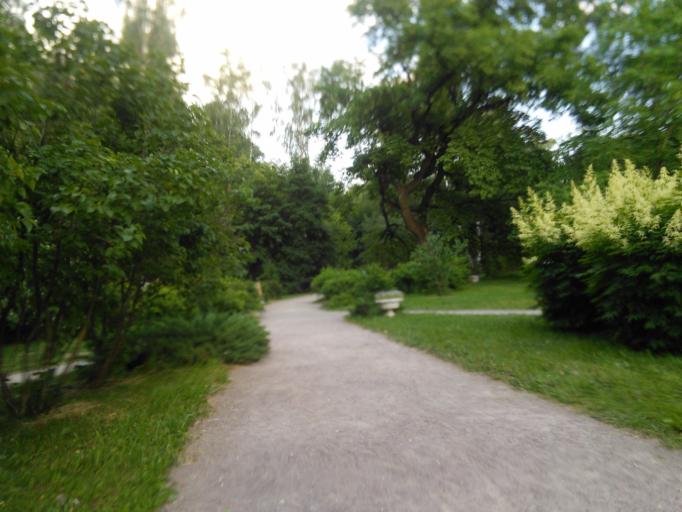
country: RU
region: Moscow
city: Sokol'niki
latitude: 55.8009
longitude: 37.6777
